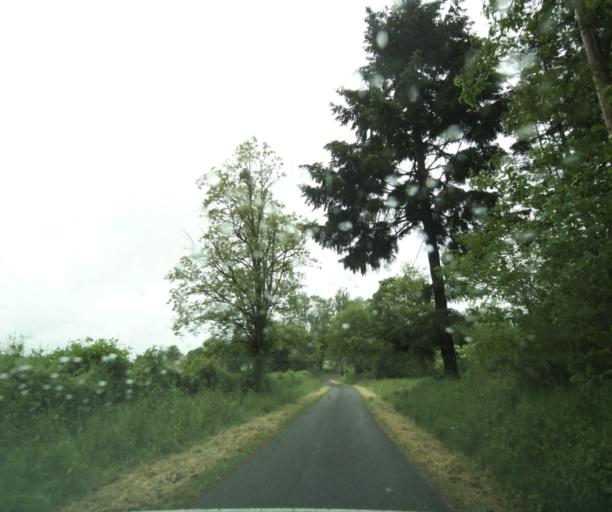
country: FR
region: Bourgogne
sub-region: Departement de Saone-et-Loire
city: Saint-Vallier
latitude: 46.4954
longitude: 4.4625
